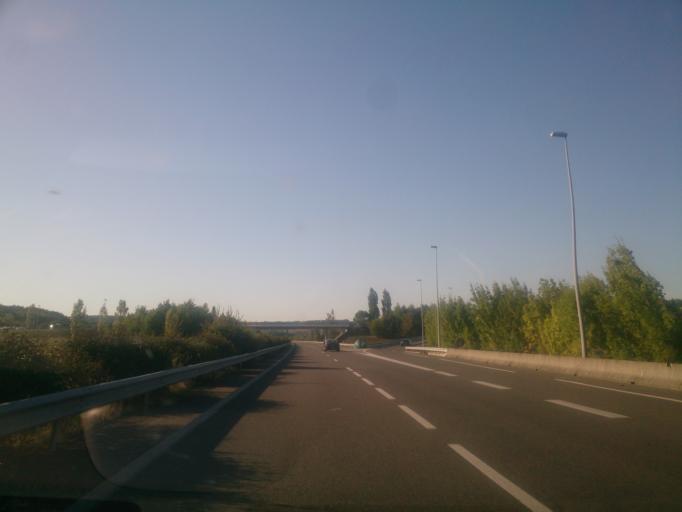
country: FR
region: Midi-Pyrenees
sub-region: Departement du Tarn-et-Garonne
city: Caussade
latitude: 44.2298
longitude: 1.5328
